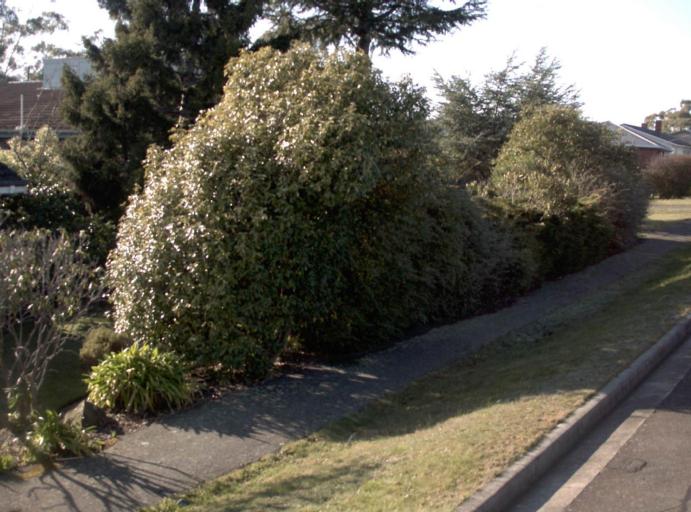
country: AU
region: Tasmania
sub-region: Launceston
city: Summerhill
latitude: -41.4647
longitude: 147.1152
